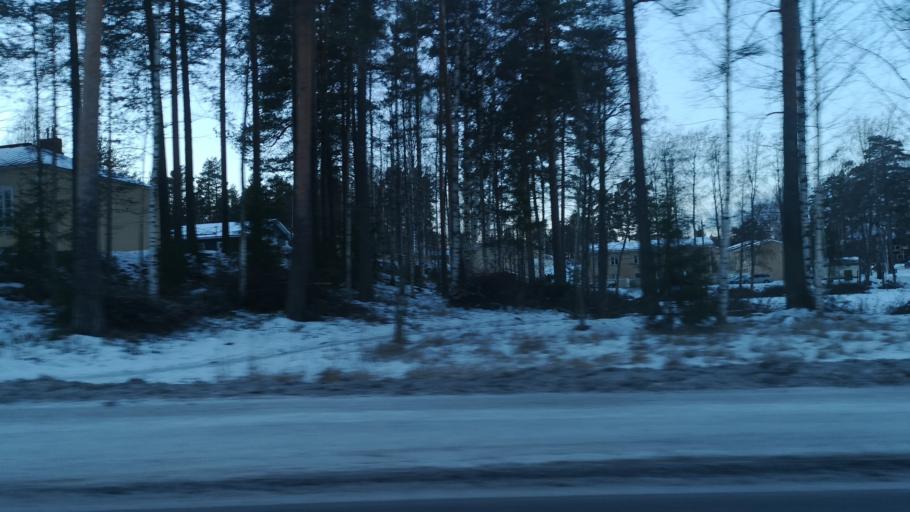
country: FI
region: Southern Savonia
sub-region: Savonlinna
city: Savonlinna
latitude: 61.8731
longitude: 28.9489
